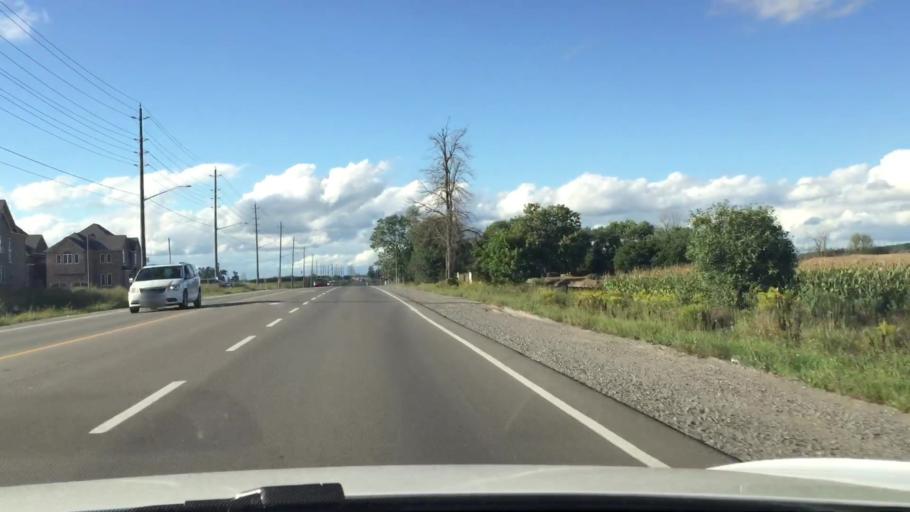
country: CA
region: Ontario
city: Oshawa
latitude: 43.9506
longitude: -78.8544
